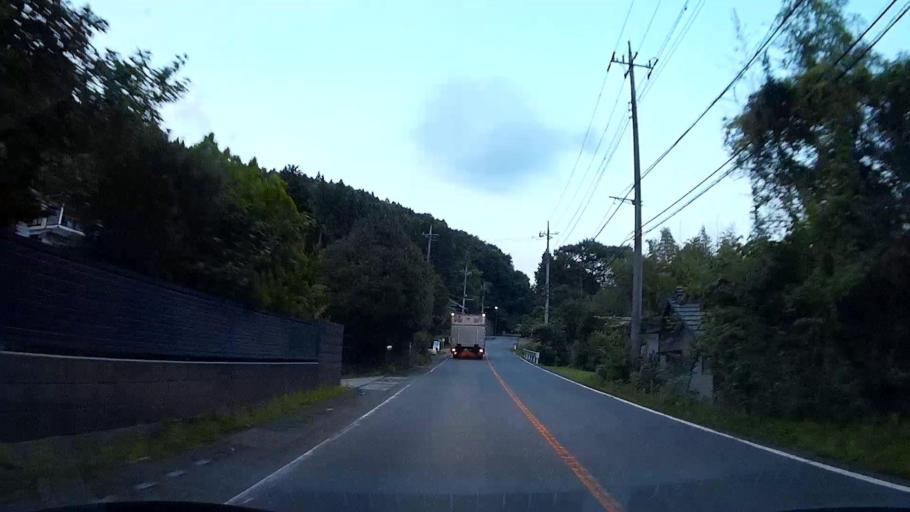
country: JP
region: Gunma
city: Annaka
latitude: 36.3891
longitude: 138.8361
